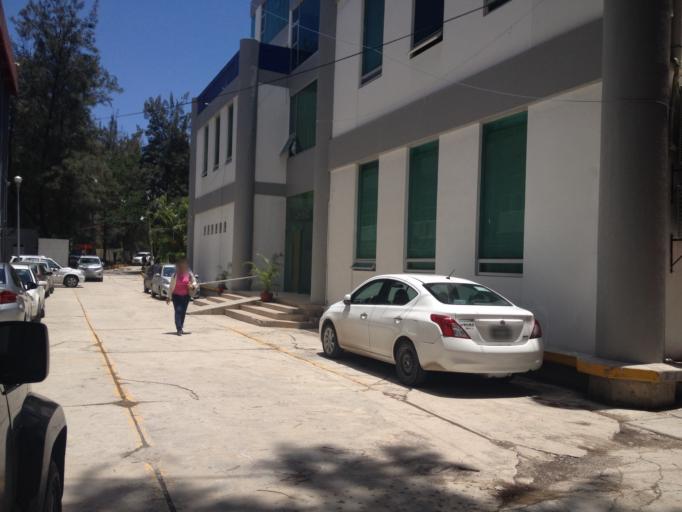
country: MX
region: Guerrero
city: Chilpancingo de los Bravos
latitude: 17.5365
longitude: -99.4951
